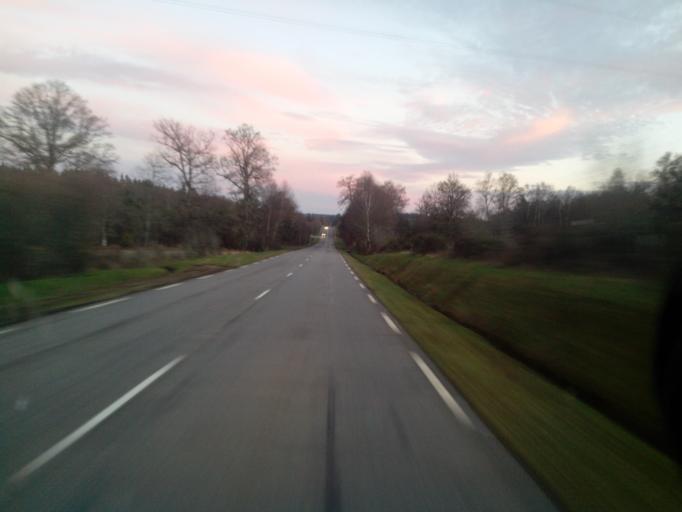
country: FR
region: Limousin
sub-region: Departement de la Correze
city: Meymac
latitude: 45.5099
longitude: 2.1955
